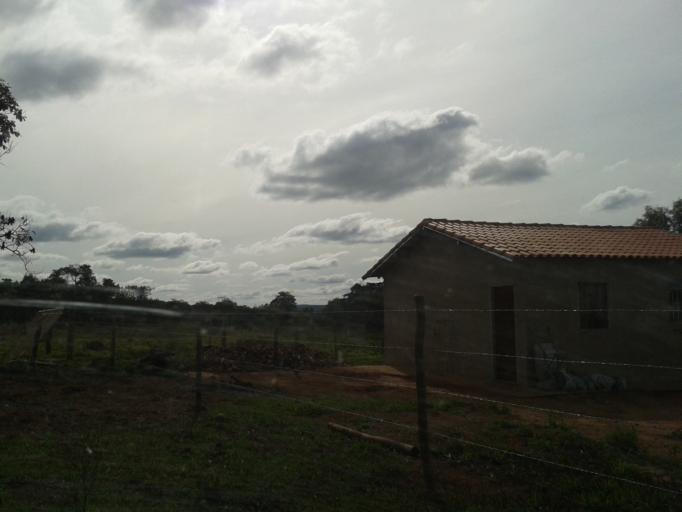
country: BR
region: Minas Gerais
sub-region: Campina Verde
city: Campina Verde
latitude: -19.4261
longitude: -49.7300
